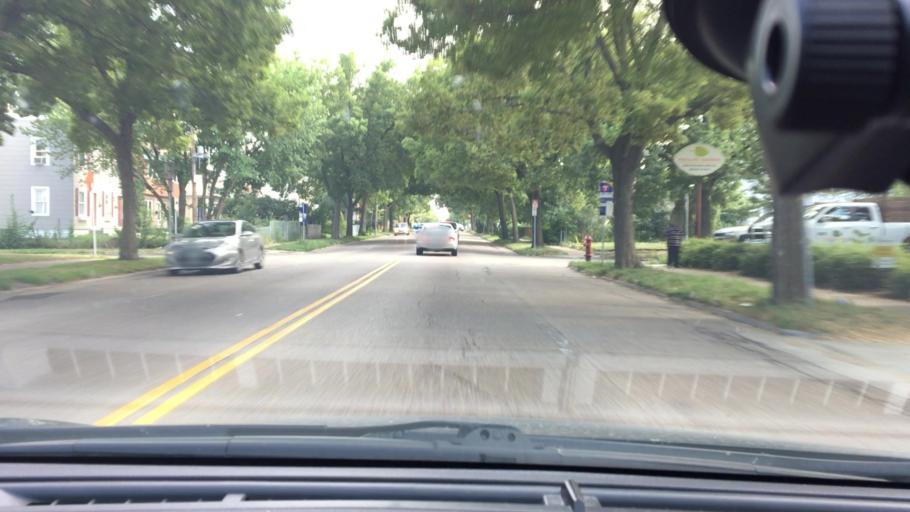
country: US
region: Minnesota
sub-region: Hennepin County
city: Minneapolis
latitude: 44.9541
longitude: -93.2474
